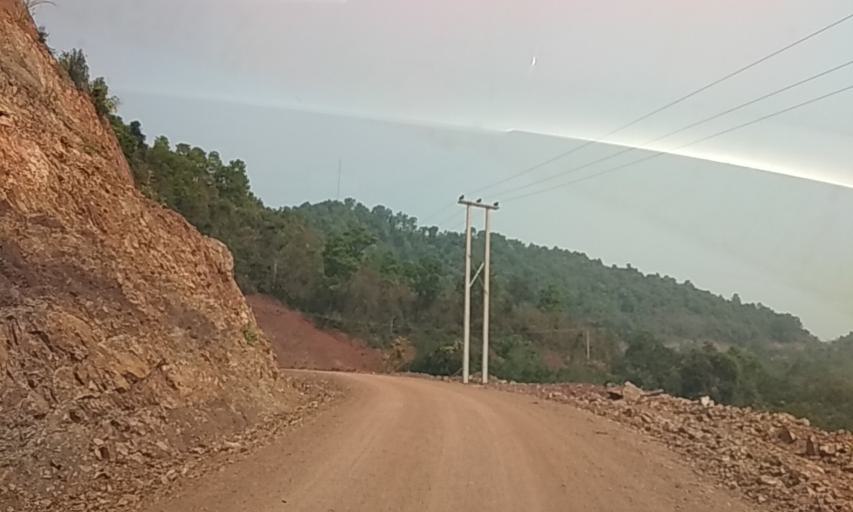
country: VN
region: Huyen Dien Bien
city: Dien Bien Phu
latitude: 21.4511
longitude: 102.7668
